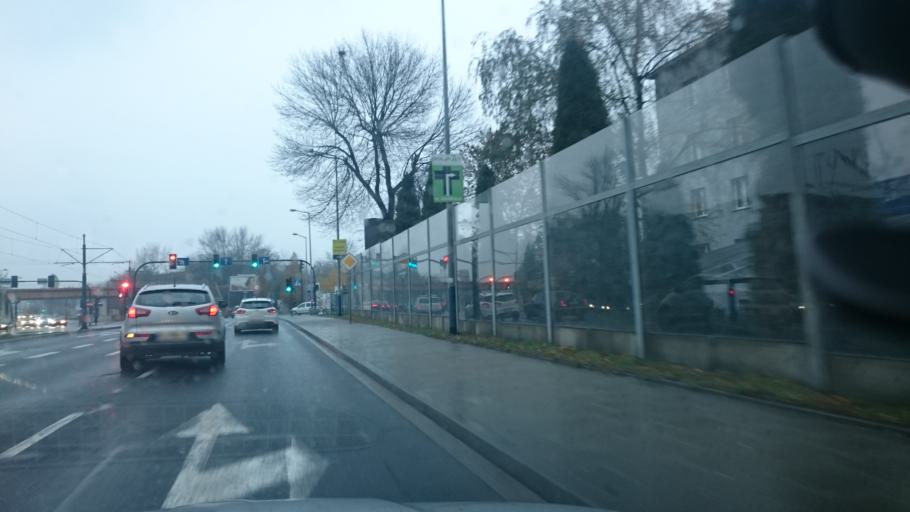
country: PL
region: Lesser Poland Voivodeship
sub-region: Krakow
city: Krakow
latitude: 50.0484
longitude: 19.9690
